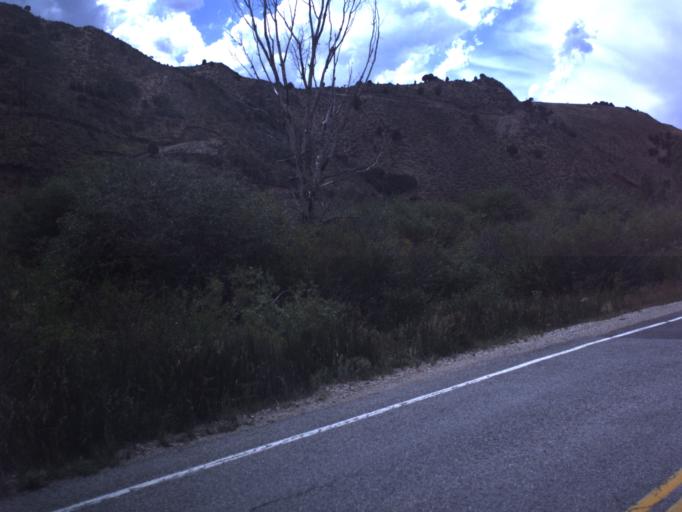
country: US
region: Utah
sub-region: Summit County
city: Oakley
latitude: 40.7542
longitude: -111.3741
